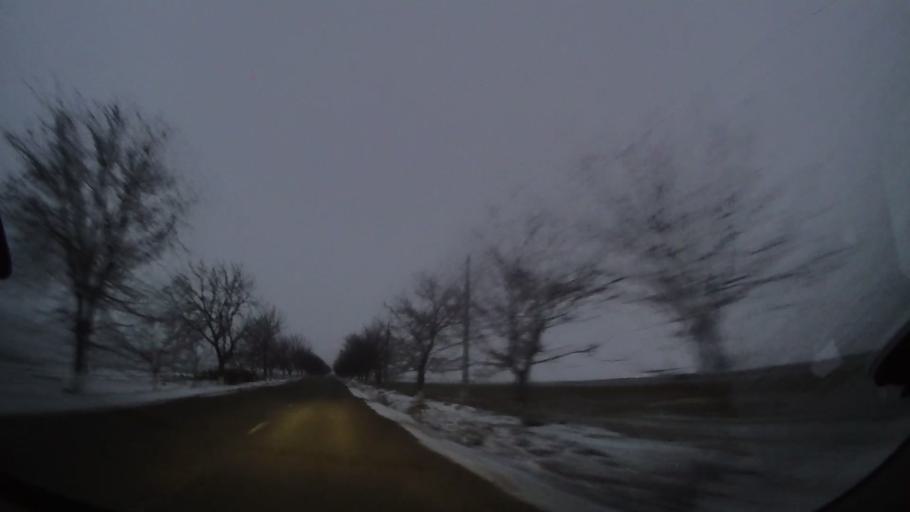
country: RO
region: Vaslui
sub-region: Comuna Dimitrie Cantemir
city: Dimitrie Cantemir
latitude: 46.5084
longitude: 28.0482
